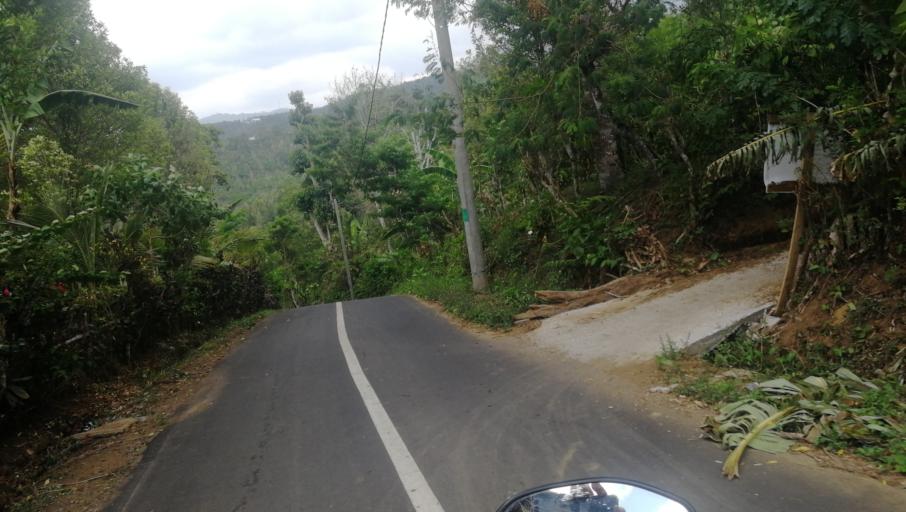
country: ID
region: Bali
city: Munduk
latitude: -8.3060
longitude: 115.0602
